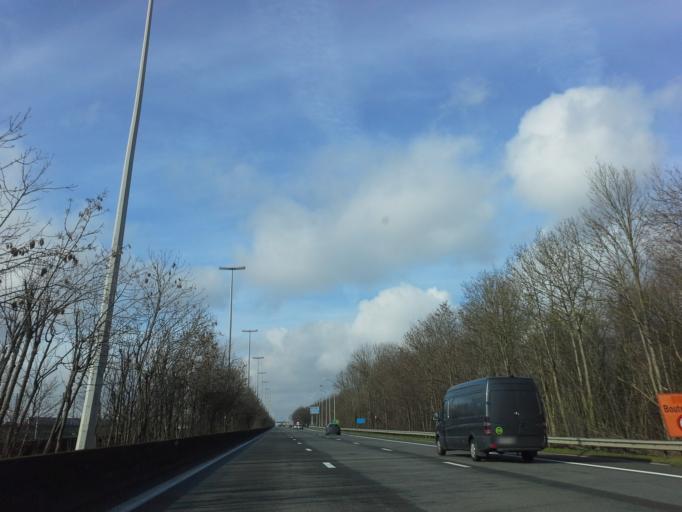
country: BE
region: Flanders
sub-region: Provincie Vlaams-Brabant
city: Boutersem
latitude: 50.8250
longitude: 4.8221
